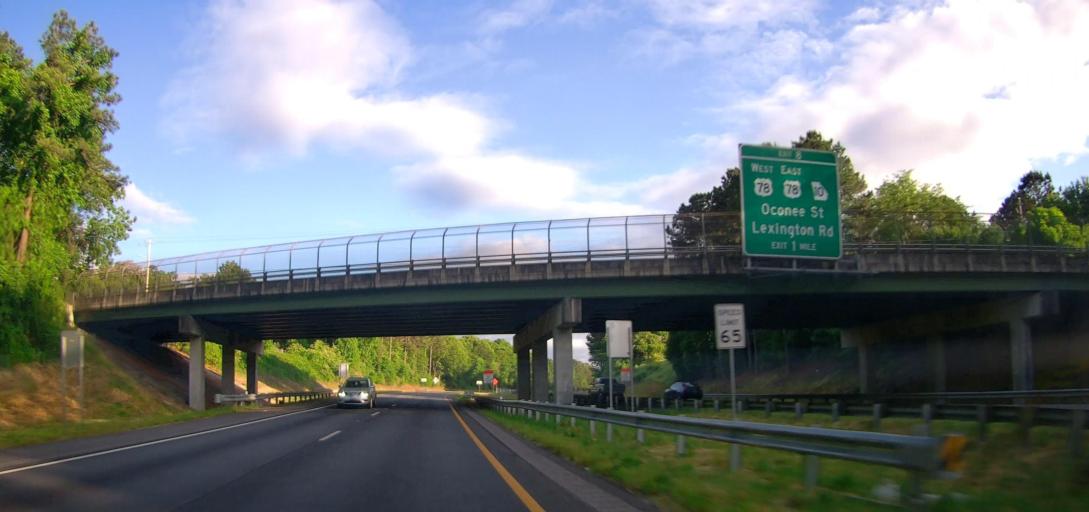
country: US
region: Georgia
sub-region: Clarke County
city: Athens
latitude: 33.9562
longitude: -83.3500
